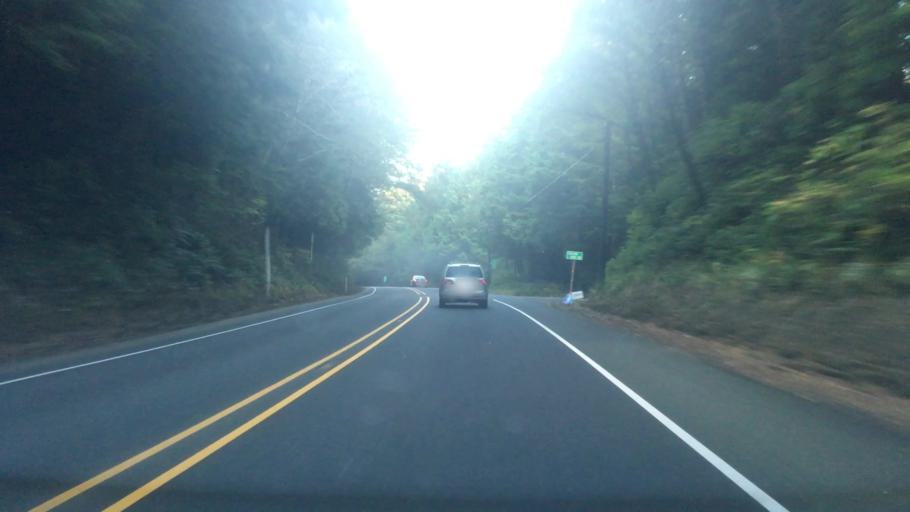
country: US
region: Oregon
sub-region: Clatsop County
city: Cannon Beach
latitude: 45.7823
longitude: -123.9569
